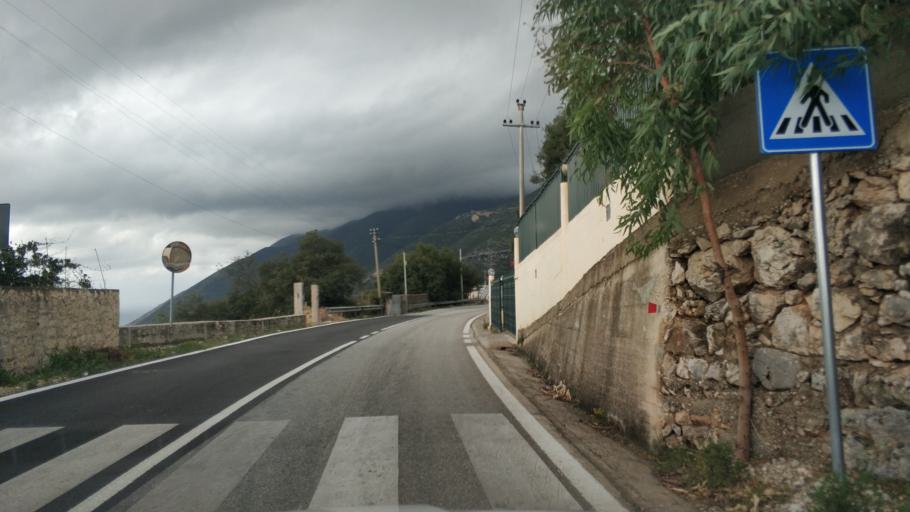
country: AL
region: Vlore
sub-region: Rrethi i Vlores
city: Vranisht
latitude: 40.1634
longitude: 19.6218
